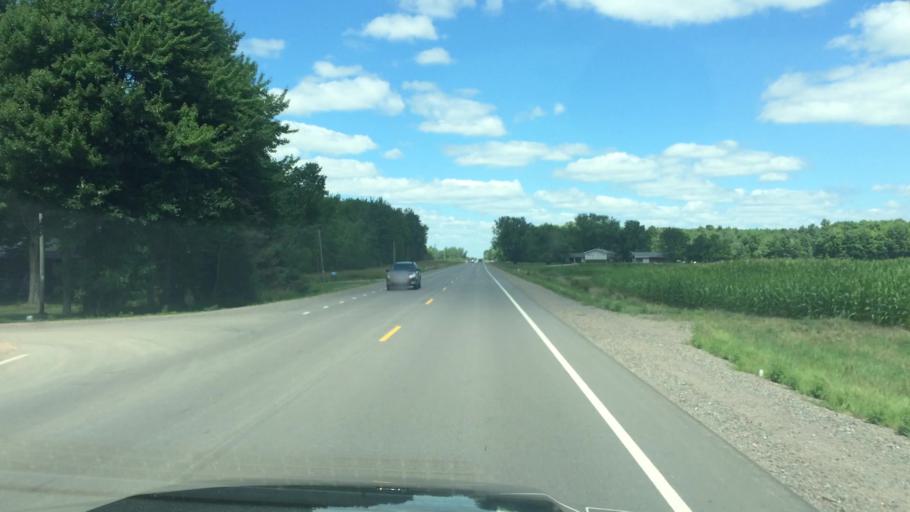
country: US
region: Wisconsin
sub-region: Clark County
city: Abbotsford
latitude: 45.0214
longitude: -90.3151
